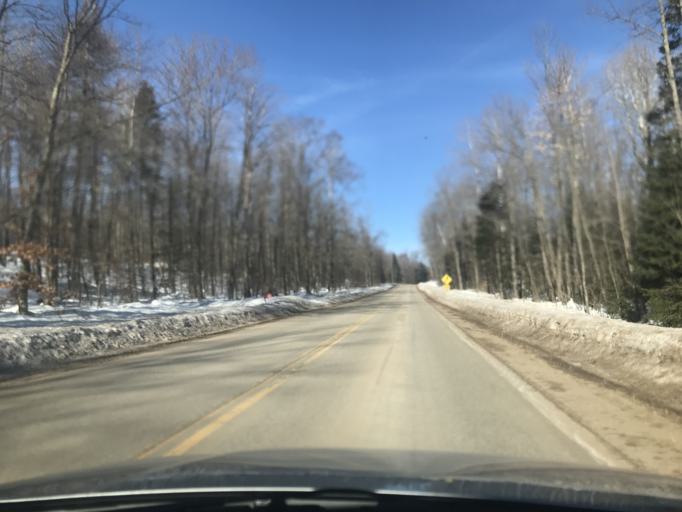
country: US
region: Michigan
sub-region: Dickinson County
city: Kingsford
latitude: 45.4127
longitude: -88.3919
